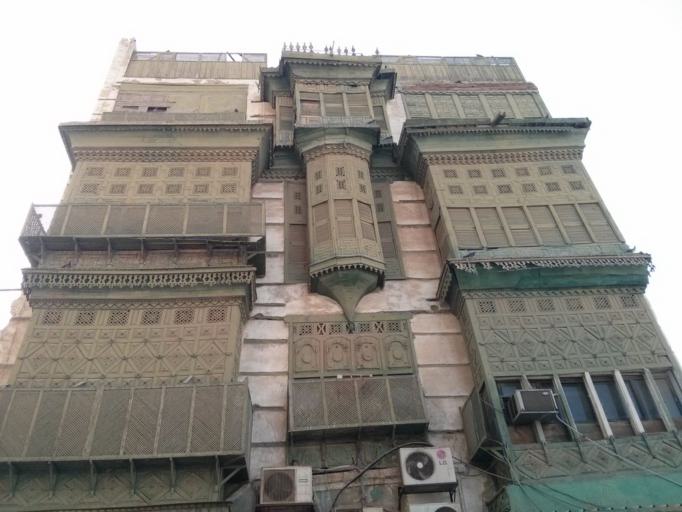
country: SA
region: Makkah
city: Jeddah
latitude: 21.4841
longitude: 39.1857
